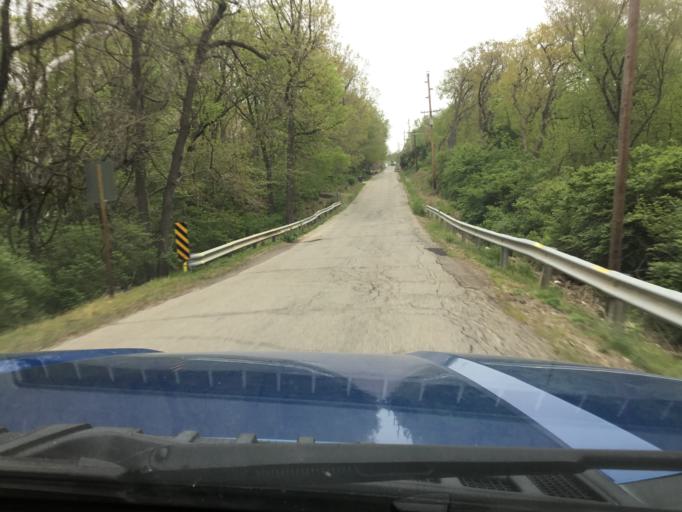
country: US
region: Kansas
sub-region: Shawnee County
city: Topeka
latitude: 39.1021
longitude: -95.6789
